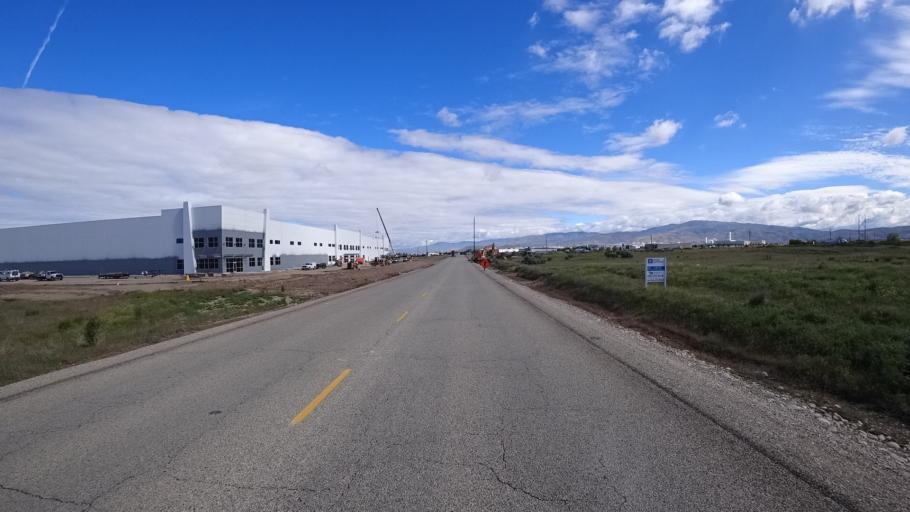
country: US
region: Idaho
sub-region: Ada County
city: Boise
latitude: 43.5142
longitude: -116.1514
